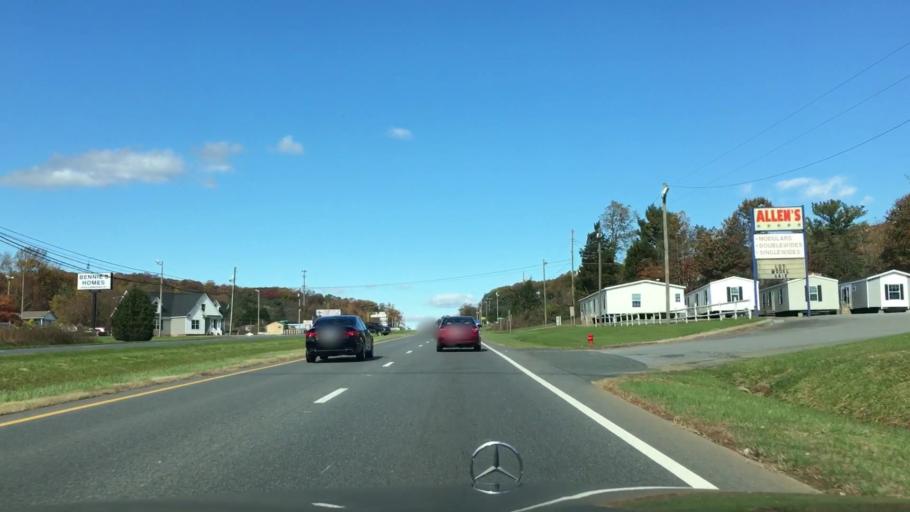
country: US
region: Virginia
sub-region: Campbell County
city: Rustburg
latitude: 37.2923
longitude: -79.1696
